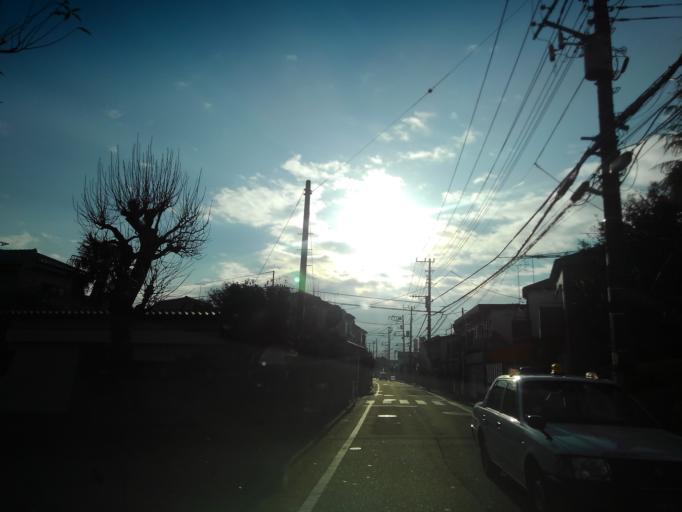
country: JP
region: Tokyo
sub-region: Machida-shi
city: Machida
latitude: 35.5431
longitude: 139.4320
